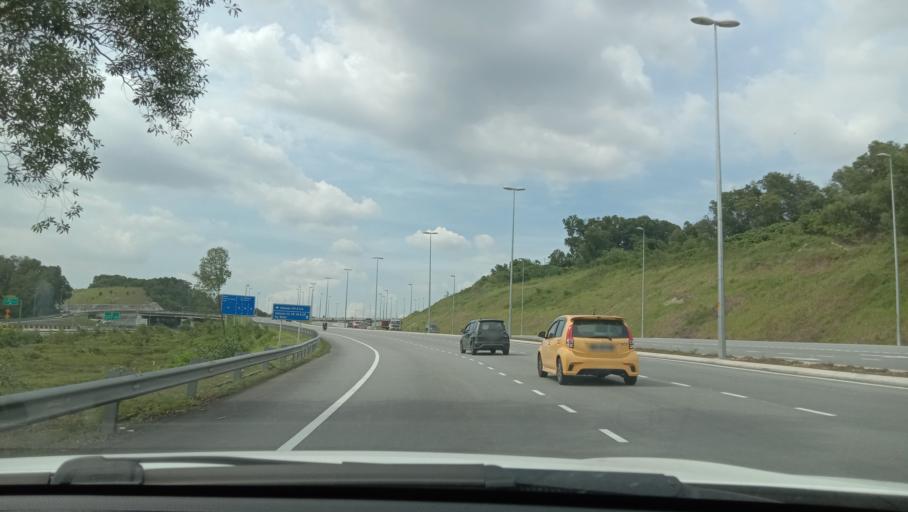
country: MY
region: Selangor
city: Kampung Baru Subang
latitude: 3.1248
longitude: 101.5290
